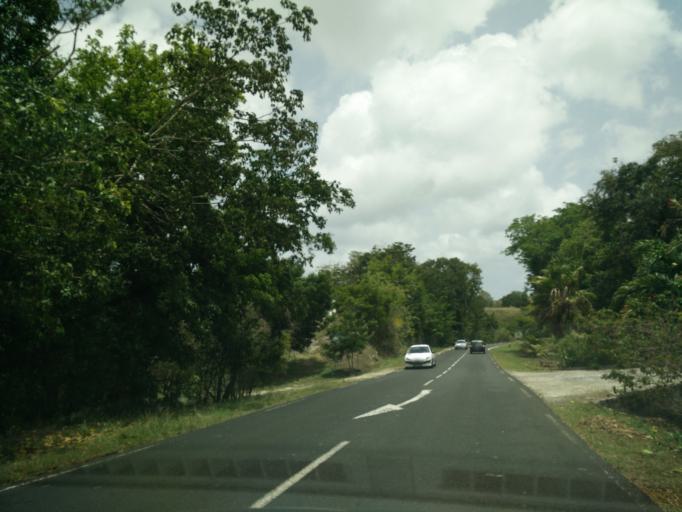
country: GP
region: Guadeloupe
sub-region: Guadeloupe
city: Petit-Canal
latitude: 16.3998
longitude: -61.5011
